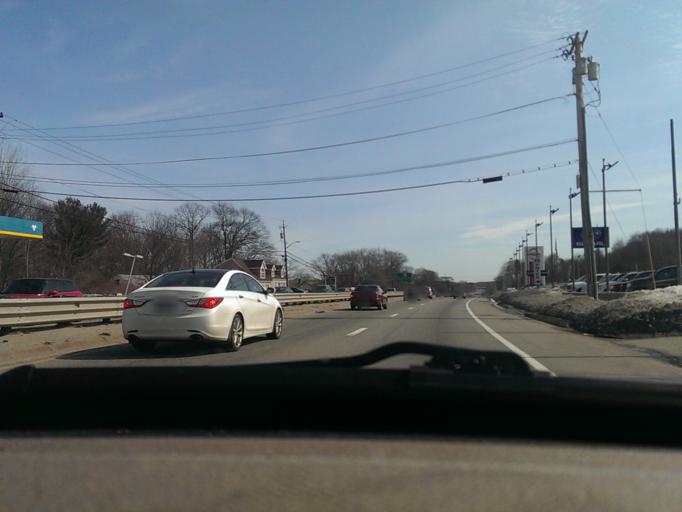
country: US
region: Rhode Island
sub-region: Providence County
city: Cumberland Hill
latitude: 41.9627
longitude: -71.4960
